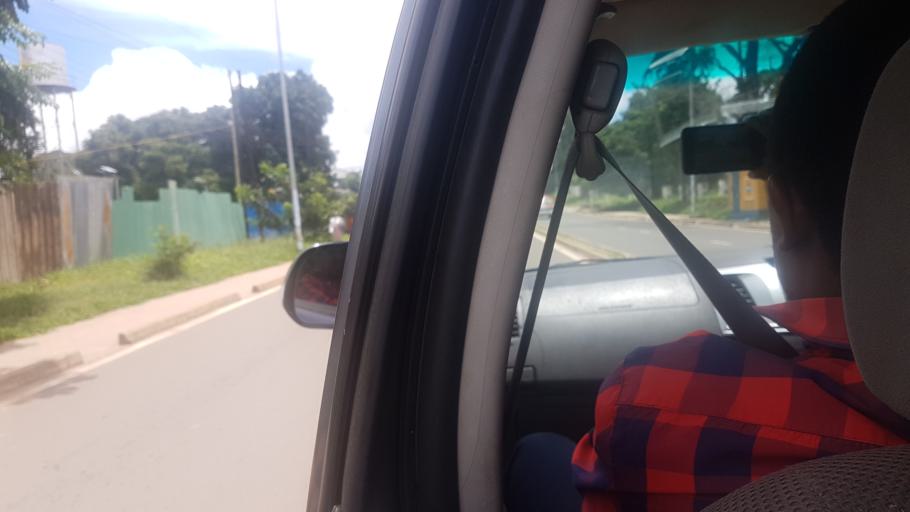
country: ZM
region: Lusaka
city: Lusaka
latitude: -15.4302
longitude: 28.3120
